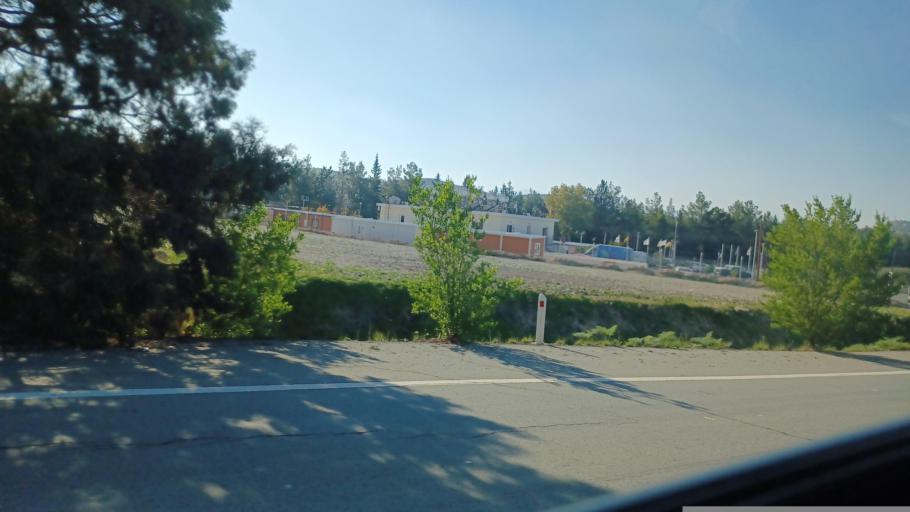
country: CY
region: Lefkosia
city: Alampra
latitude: 35.0047
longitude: 33.3953
